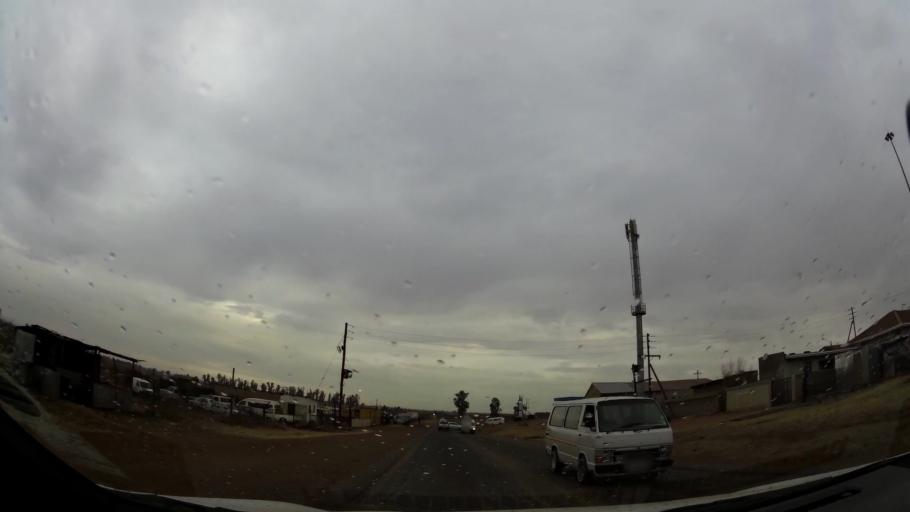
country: ZA
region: Gauteng
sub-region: Ekurhuleni Metropolitan Municipality
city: Germiston
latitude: -26.3758
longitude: 28.1737
